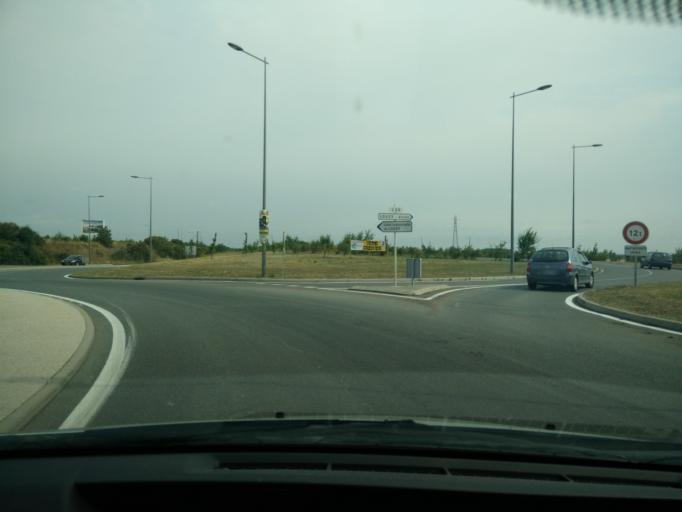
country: FR
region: Poitou-Charentes
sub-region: Departement des Deux-Sevres
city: Louzy
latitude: 46.9989
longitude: -0.1940
